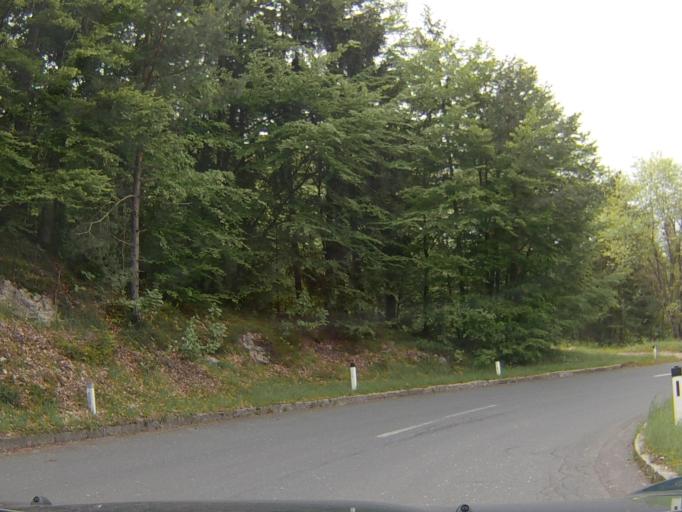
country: AT
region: Carinthia
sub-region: Villach Stadt
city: Villach
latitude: 46.6021
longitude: 13.8056
